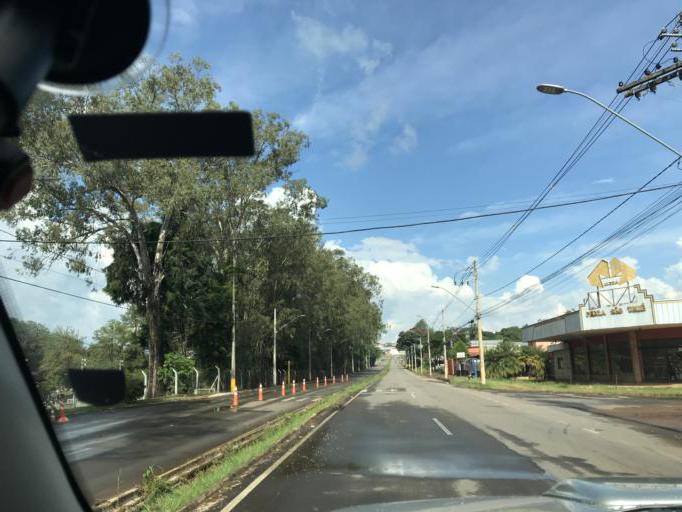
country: BR
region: Minas Gerais
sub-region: Tres Coracoes
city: Tres Coracoes
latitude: -21.6614
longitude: -45.2859
